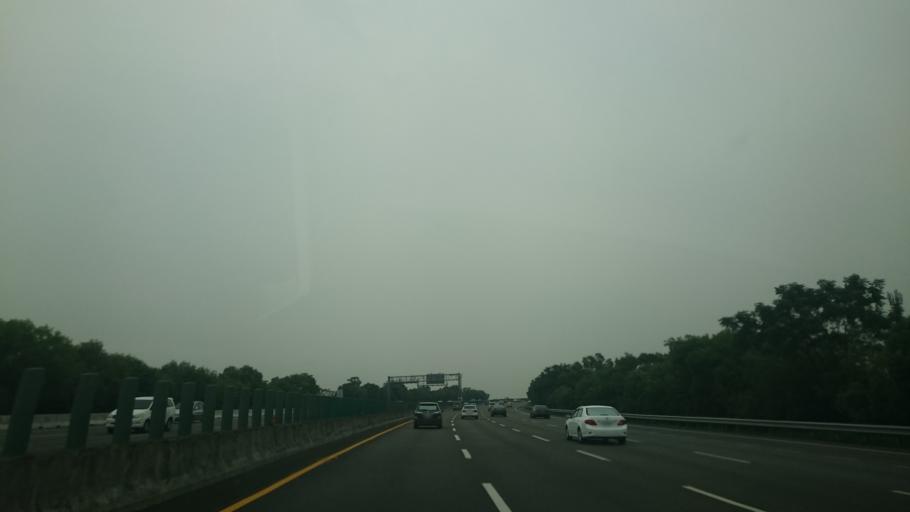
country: TW
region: Taiwan
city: Zhongxing New Village
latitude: 23.9646
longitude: 120.6496
